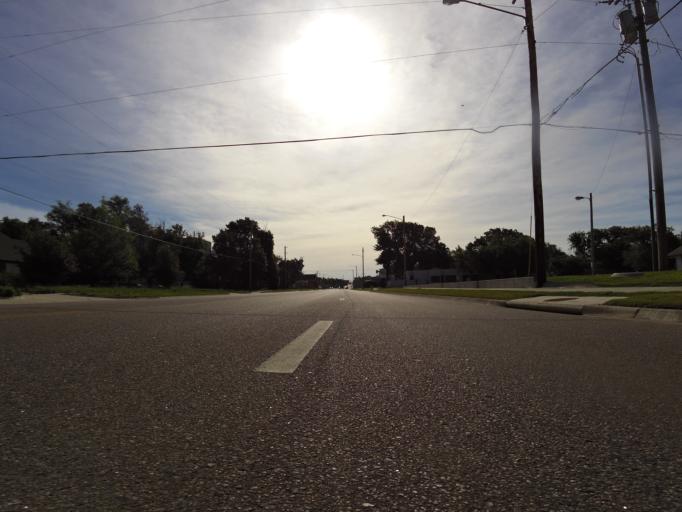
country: US
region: Kansas
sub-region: Sedgwick County
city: Wichita
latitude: 37.7080
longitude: -97.3112
